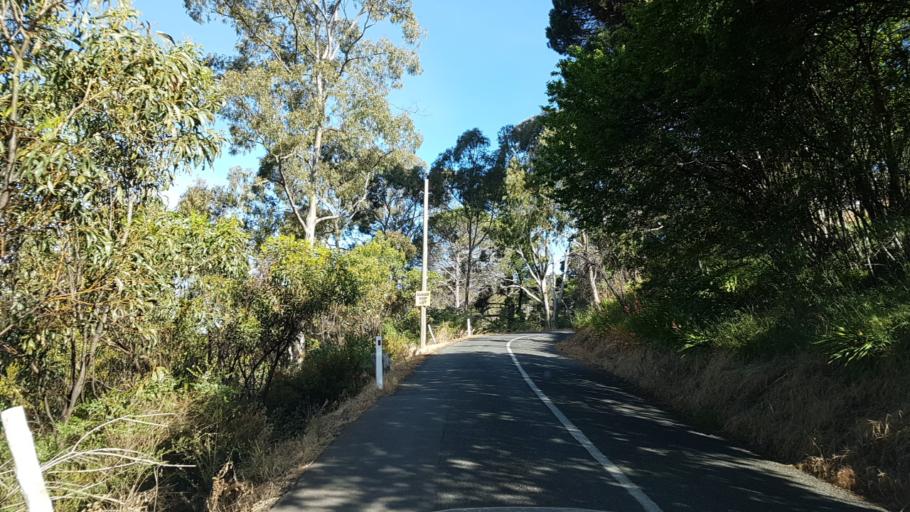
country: AU
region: South Australia
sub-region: Adelaide Hills
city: Adelaide Hills
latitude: -34.9102
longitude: 138.7673
